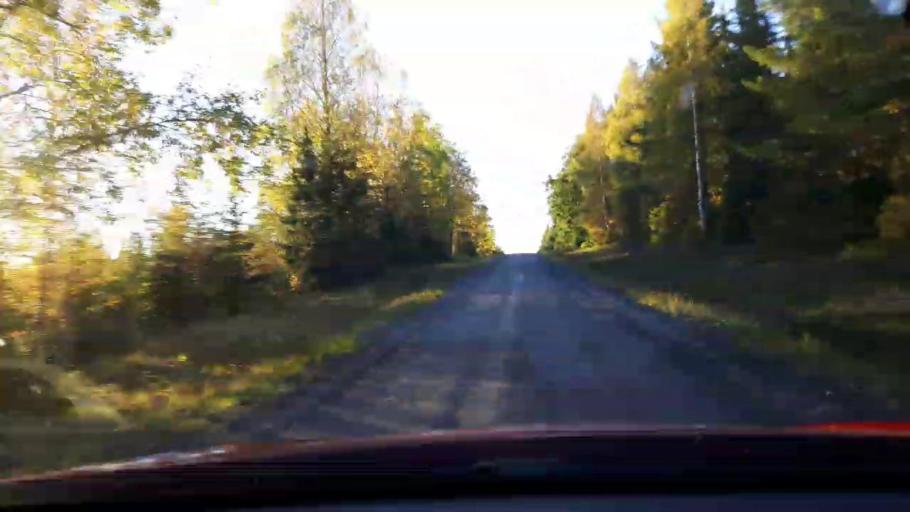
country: SE
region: Jaemtland
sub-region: Krokoms Kommun
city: Krokom
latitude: 63.4144
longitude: 14.6197
